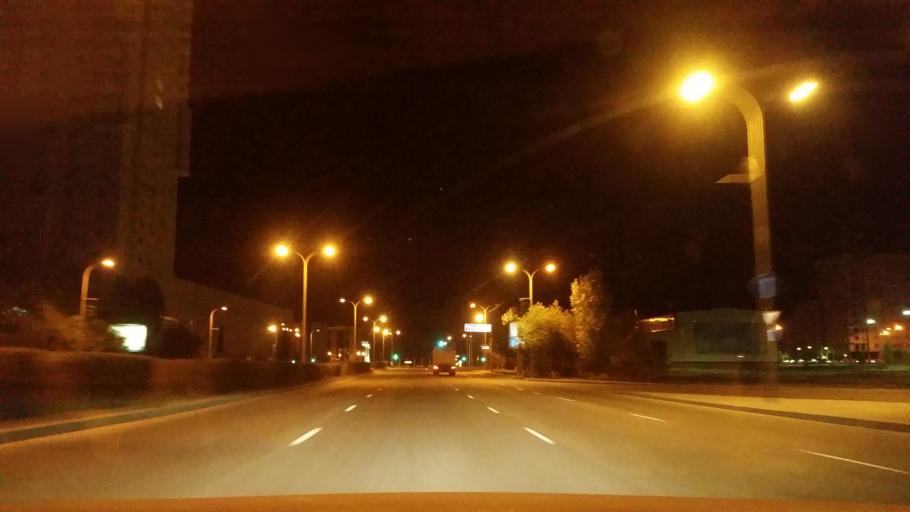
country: KZ
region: Astana Qalasy
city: Astana
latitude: 51.1178
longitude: 71.4628
